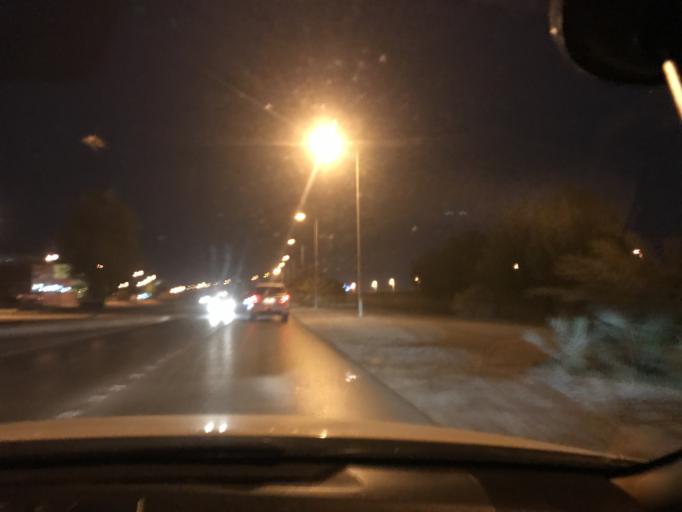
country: BH
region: Muharraq
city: Al Muharraq
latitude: 26.2811
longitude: 50.6209
